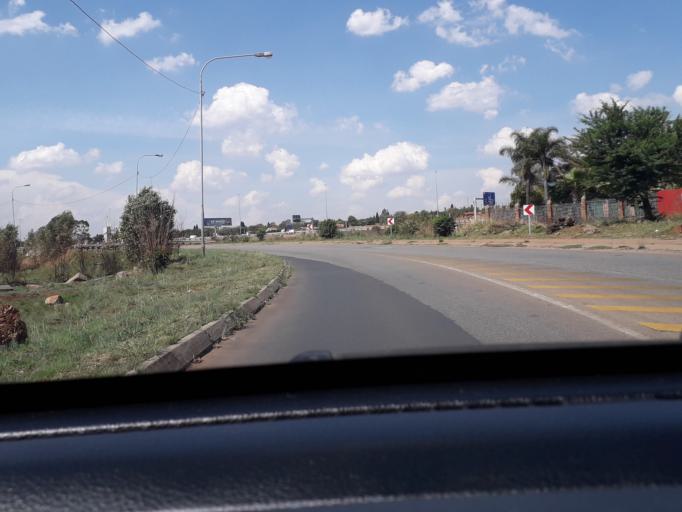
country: ZA
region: Gauteng
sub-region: City of Tshwane Metropolitan Municipality
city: Centurion
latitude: -25.8501
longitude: 28.2256
